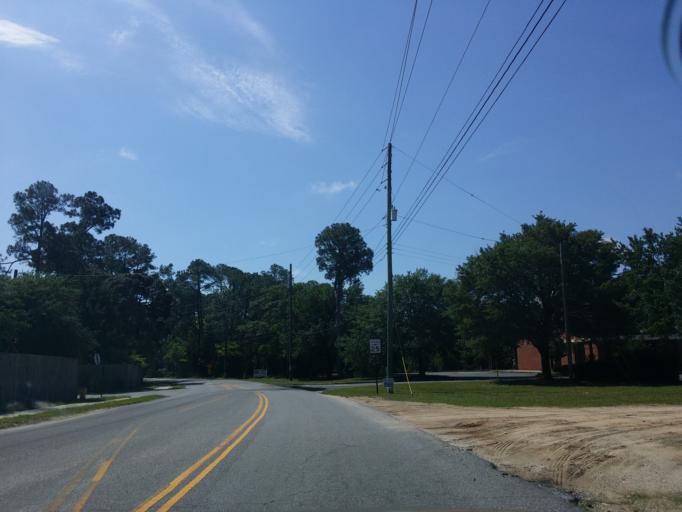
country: US
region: Florida
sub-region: Escambia County
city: Warrington
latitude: 30.3885
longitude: -87.2727
